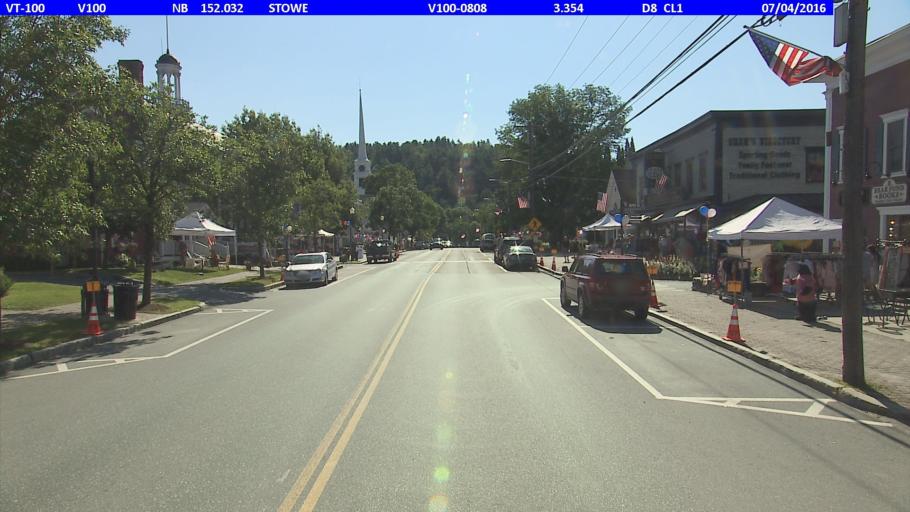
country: US
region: Vermont
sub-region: Lamoille County
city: Morristown
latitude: 44.4654
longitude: -72.6868
